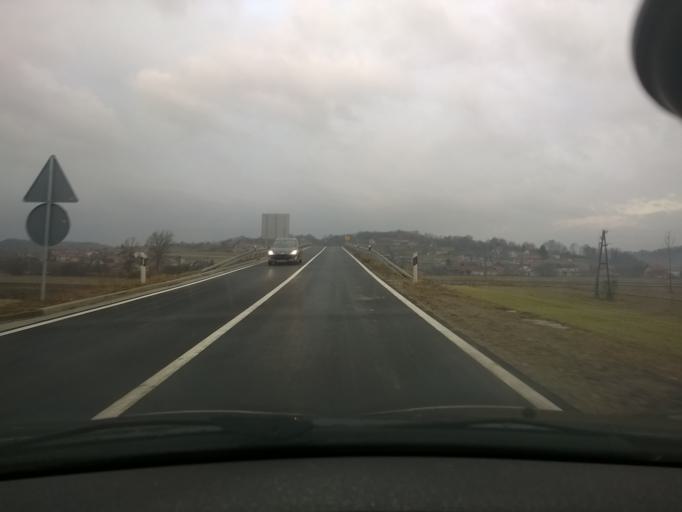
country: HR
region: Krapinsko-Zagorska
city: Bedekovcina
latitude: 46.0363
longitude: 15.9851
